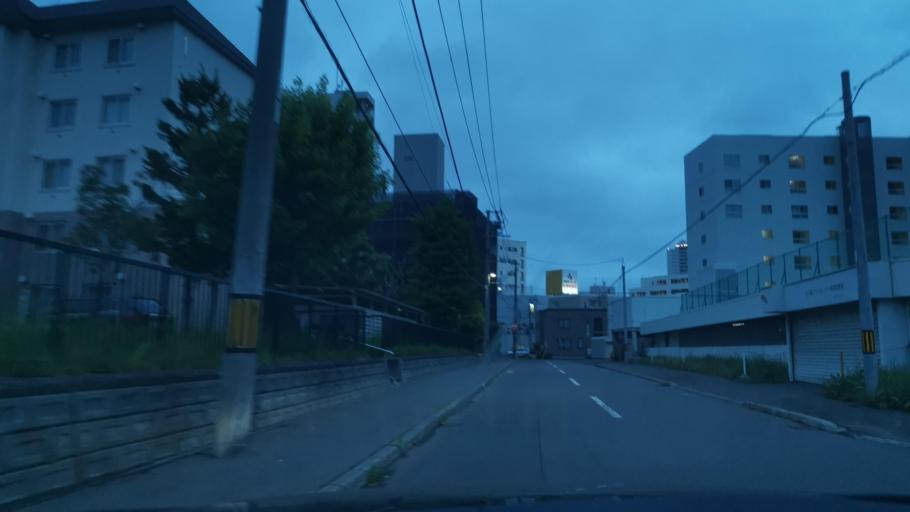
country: JP
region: Hokkaido
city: Sapporo
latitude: 43.0628
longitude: 141.3123
